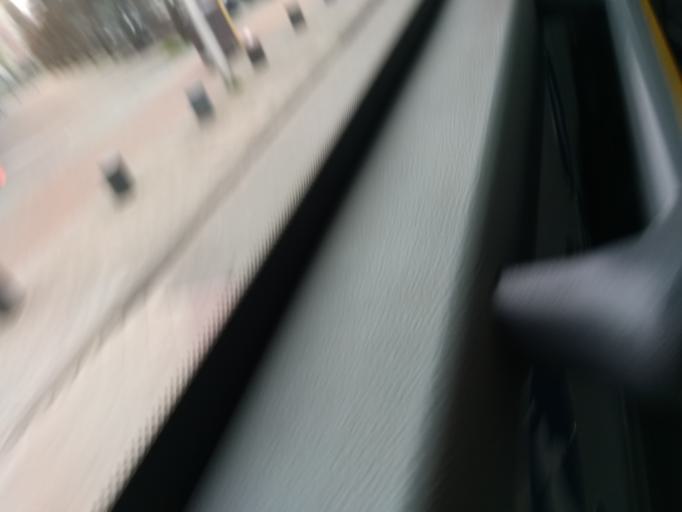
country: FR
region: Picardie
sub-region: Departement de l'Oise
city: Venette
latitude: 49.4068
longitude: 2.8029
